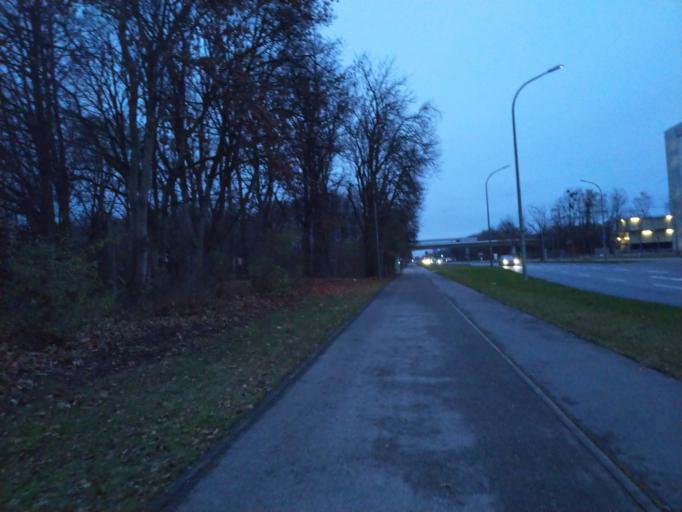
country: DE
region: Bavaria
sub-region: Upper Bavaria
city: Oberschleissheim
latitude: 48.1968
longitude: 11.5647
